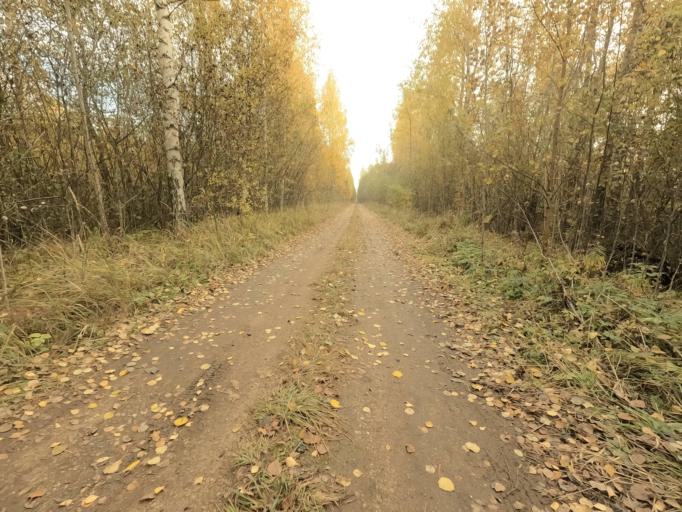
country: RU
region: Novgorod
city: Pankovka
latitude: 58.8786
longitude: 30.8571
